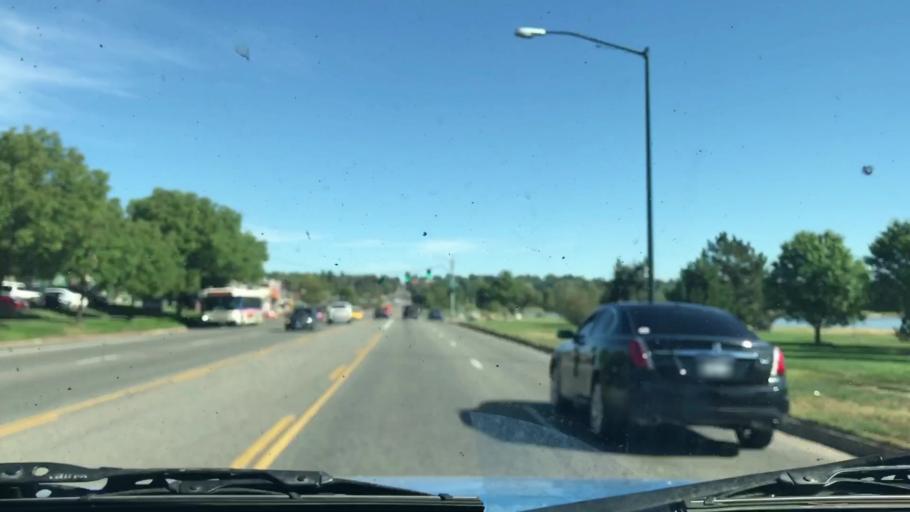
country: US
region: Colorado
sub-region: Jefferson County
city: Edgewater
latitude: 39.7464
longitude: -105.0532
